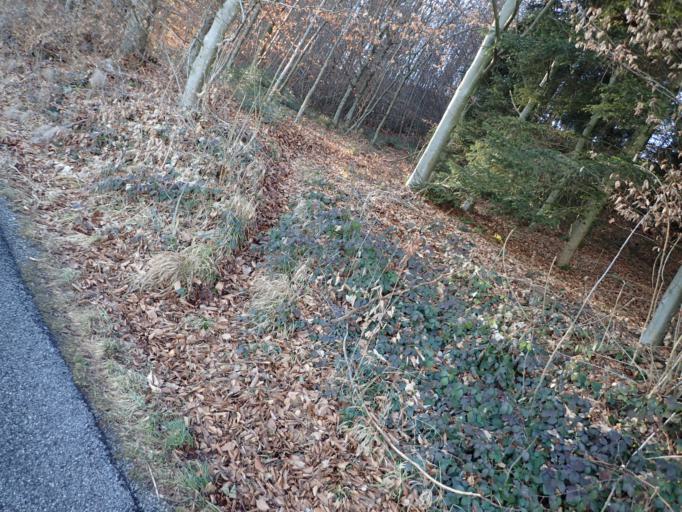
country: AT
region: Salzburg
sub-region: Politischer Bezirk Salzburg-Umgebung
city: Mattsee
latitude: 47.9519
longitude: 13.1201
